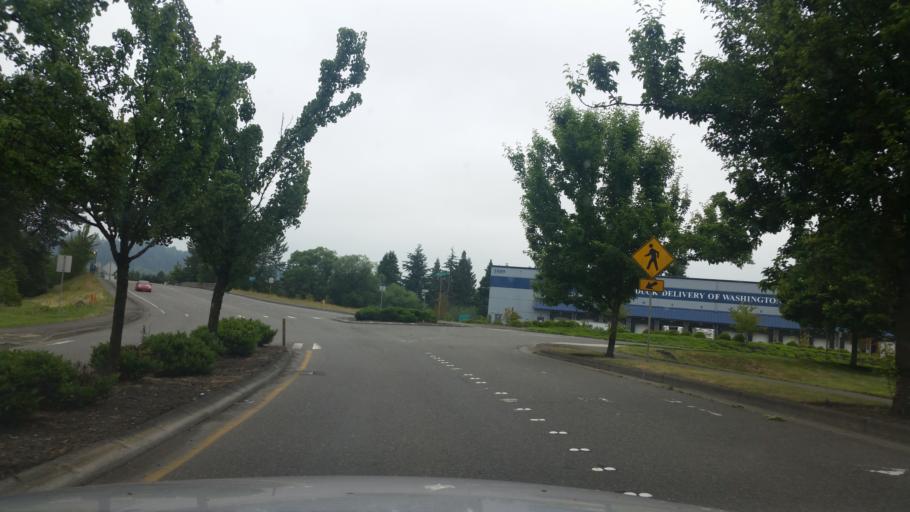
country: US
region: Washington
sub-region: Pierce County
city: Sumner
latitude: 47.2154
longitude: -122.2369
